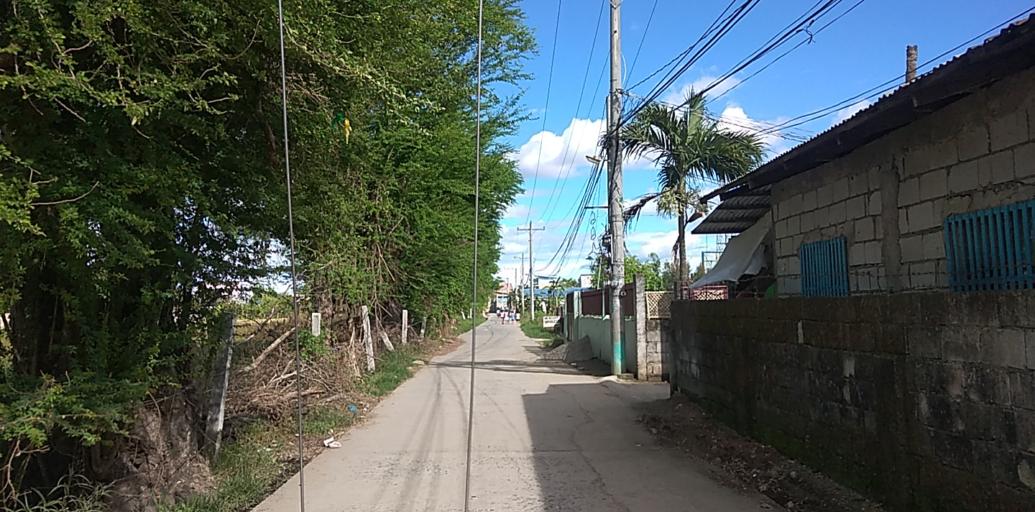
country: PH
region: Central Luzon
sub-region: Province of Pampanga
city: Arayat
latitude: 15.1388
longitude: 120.7704
